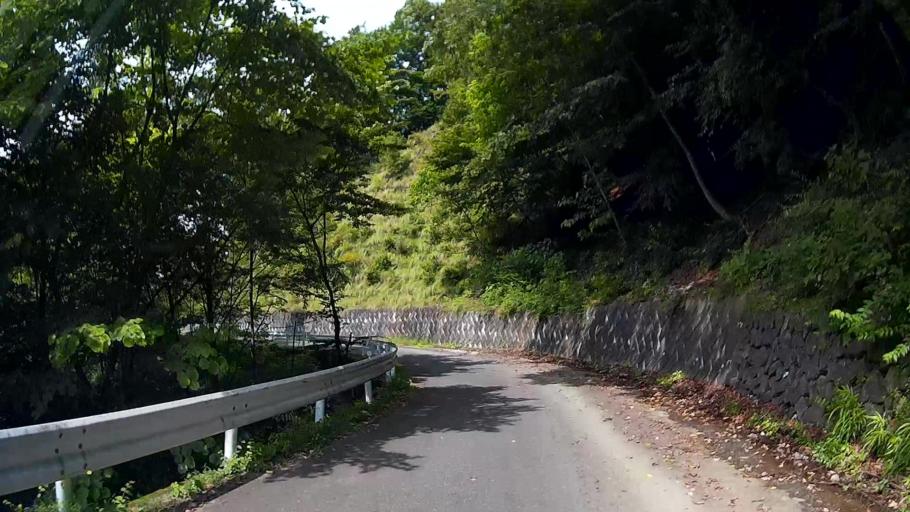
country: JP
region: Saitama
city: Chichibu
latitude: 35.8907
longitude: 139.1114
